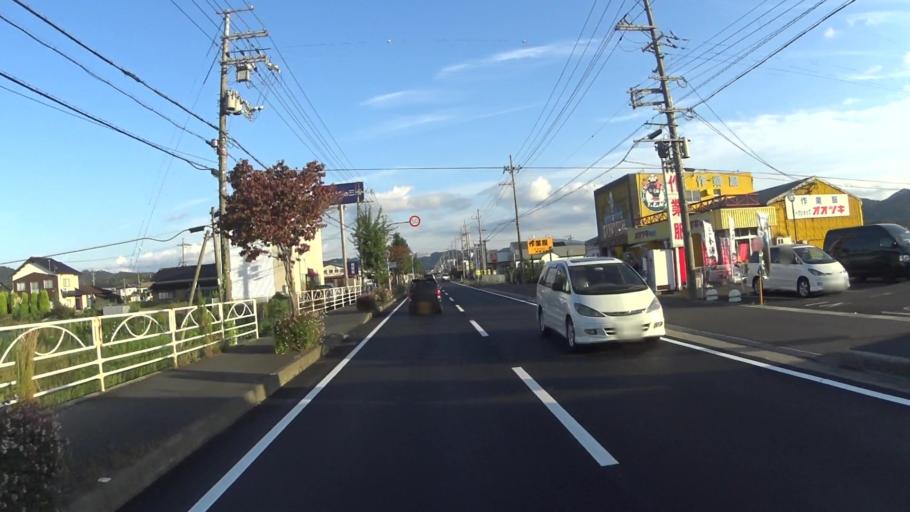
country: JP
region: Kyoto
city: Miyazu
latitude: 35.6043
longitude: 135.0837
